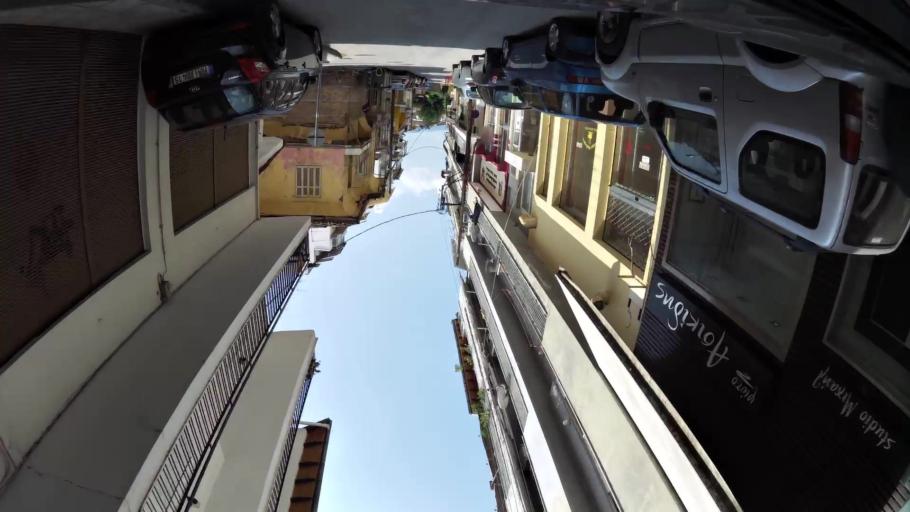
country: GR
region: Central Macedonia
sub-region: Nomos Imathias
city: Veroia
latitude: 40.5203
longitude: 22.2026
